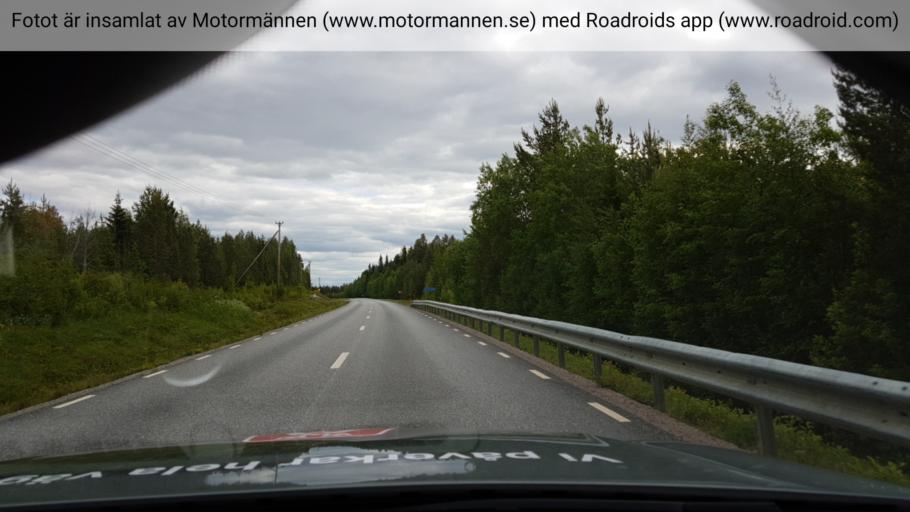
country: SE
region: Jaemtland
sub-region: Stroemsunds Kommun
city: Stroemsund
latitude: 63.9543
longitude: 15.4818
